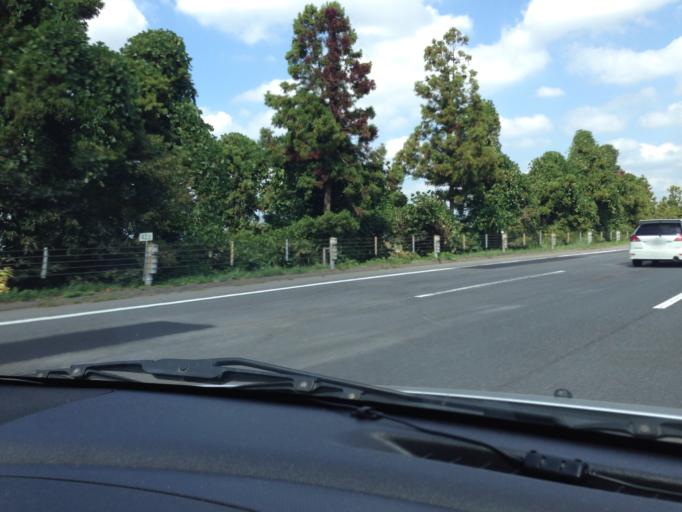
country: JP
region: Ibaraki
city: Naka
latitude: 36.0876
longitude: 140.1573
